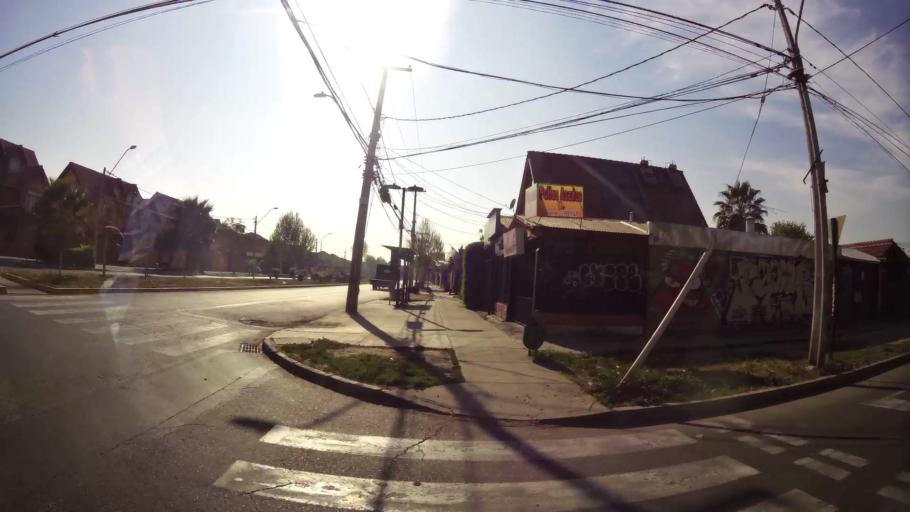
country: CL
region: Santiago Metropolitan
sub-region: Provincia de Santiago
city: Lo Prado
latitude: -33.4539
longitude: -70.7657
